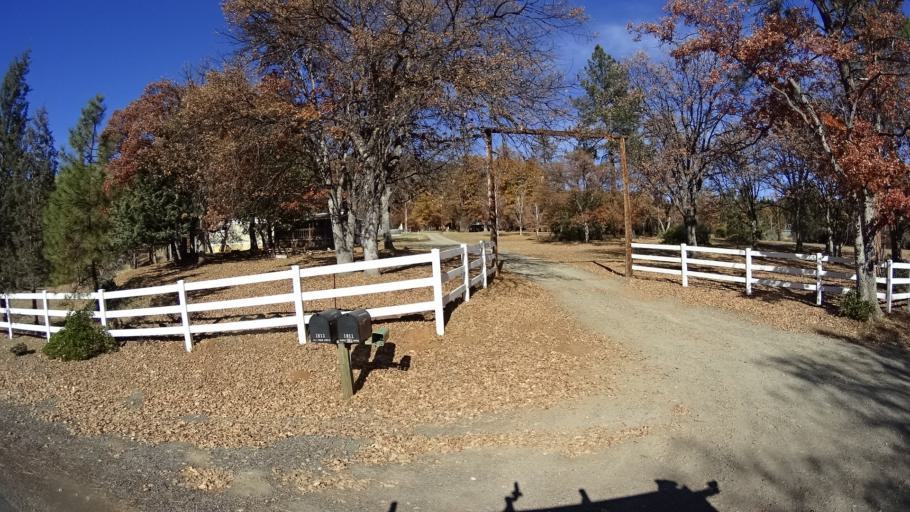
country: US
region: California
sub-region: Siskiyou County
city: Yreka
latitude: 41.7168
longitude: -122.6647
